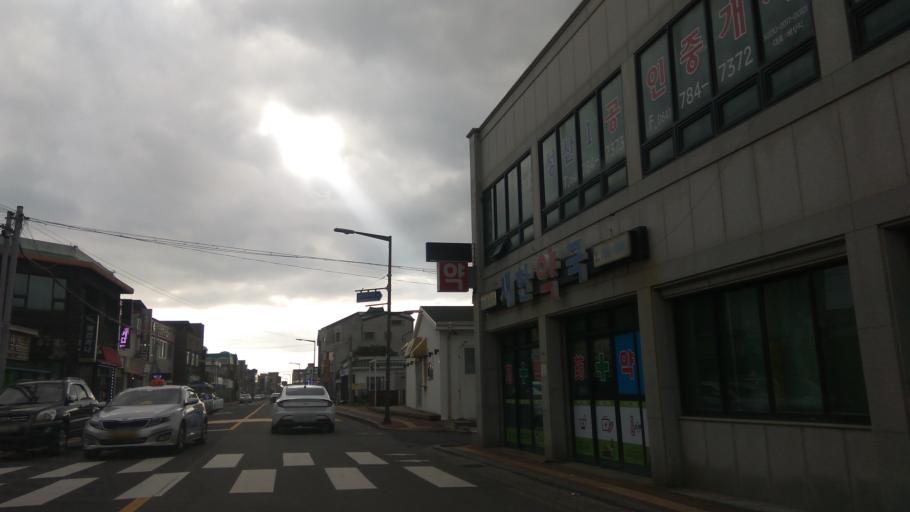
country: KR
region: Jeju-do
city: Jeju-si
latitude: 33.4633
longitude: 126.9334
